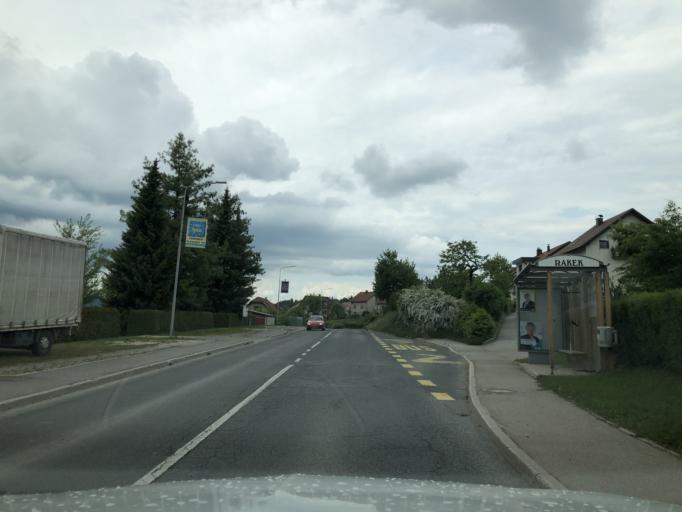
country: SI
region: Cerknica
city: Rakek
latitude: 45.8087
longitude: 14.3282
